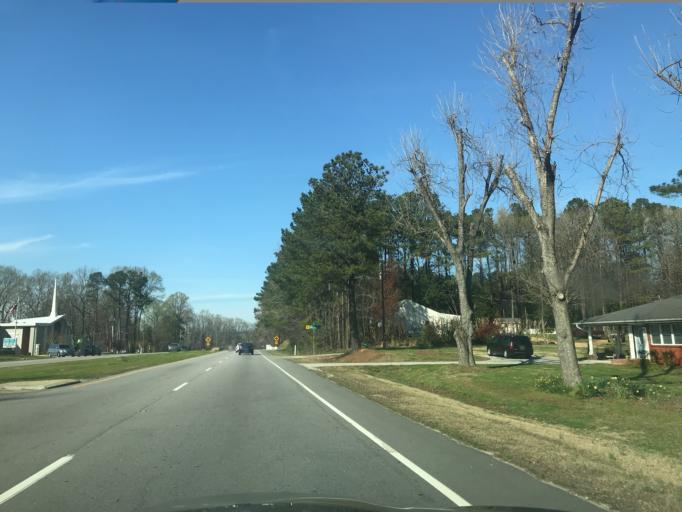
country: US
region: North Carolina
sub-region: Wake County
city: Garner
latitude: 35.6808
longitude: -78.6860
